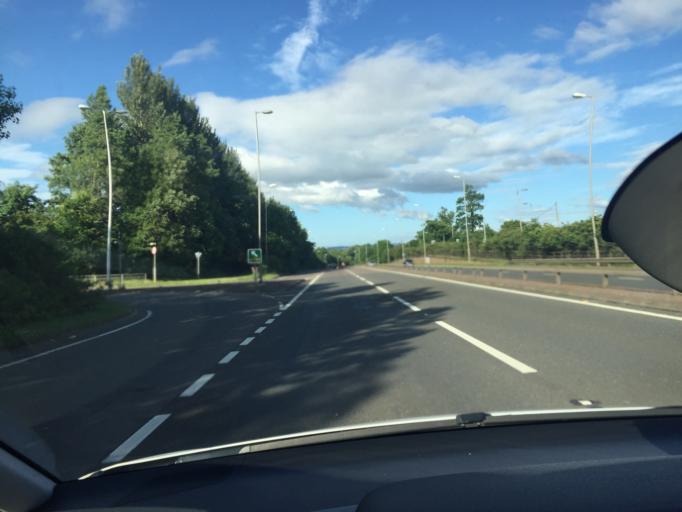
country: GB
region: Scotland
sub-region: South Lanarkshire
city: Bothwell
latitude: 55.7924
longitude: -4.0712
